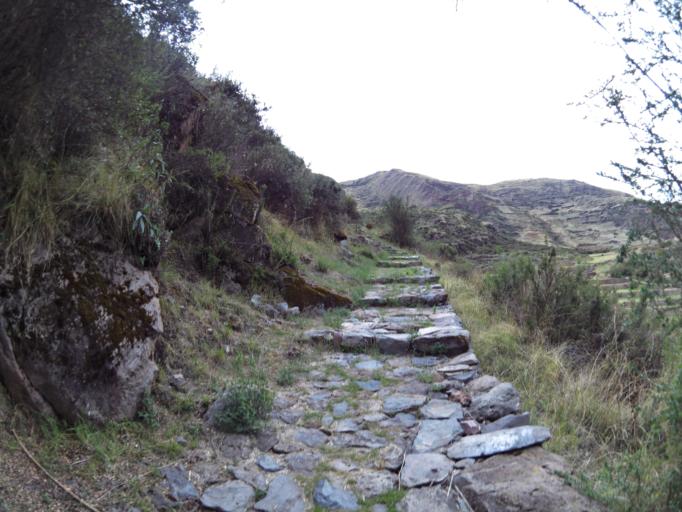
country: PE
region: Cusco
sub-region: Provincia de Quispicanchis
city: Oropesa
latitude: -13.5694
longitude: -71.7831
